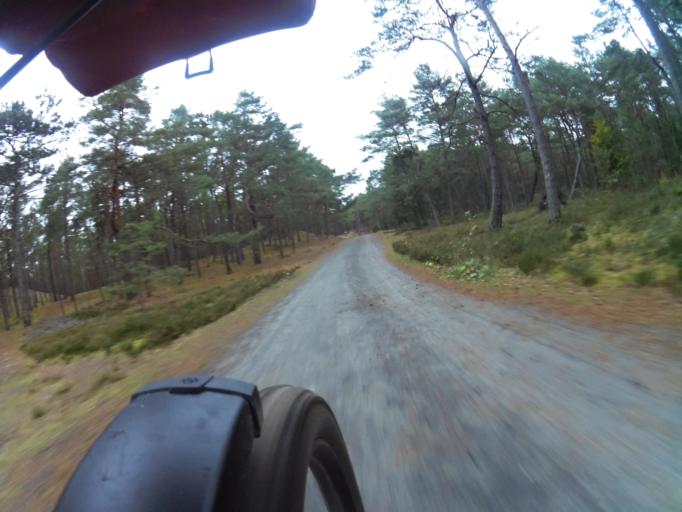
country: PL
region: Pomeranian Voivodeship
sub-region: Powiat wejherowski
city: Choczewo
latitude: 54.7840
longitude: 17.7429
